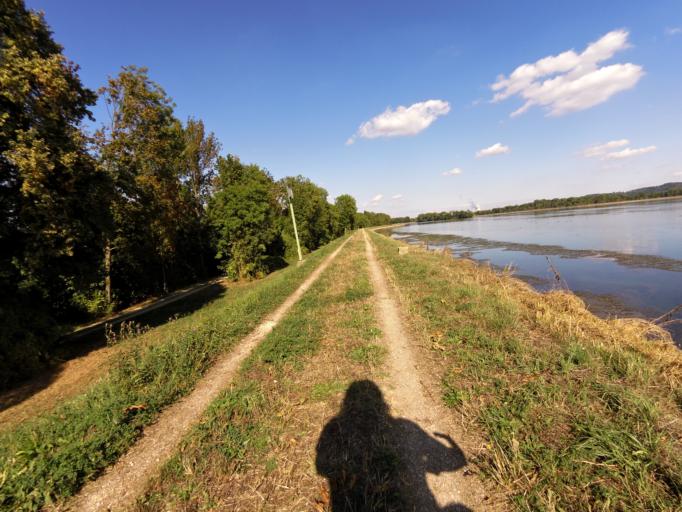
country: DE
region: Bavaria
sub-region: Lower Bavaria
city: Stallwang
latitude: 48.5774
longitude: 12.2052
